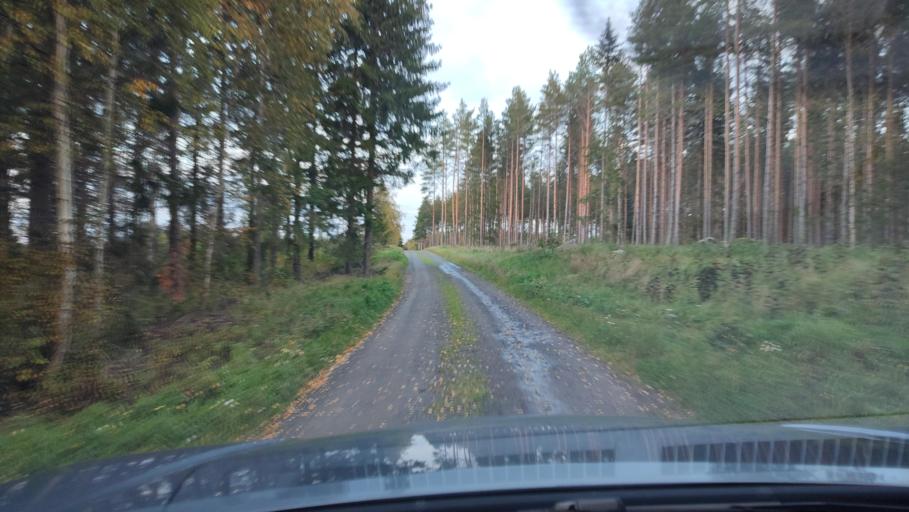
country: FI
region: Ostrobothnia
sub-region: Sydosterbotten
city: Kristinestad
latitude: 62.2466
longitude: 21.4531
